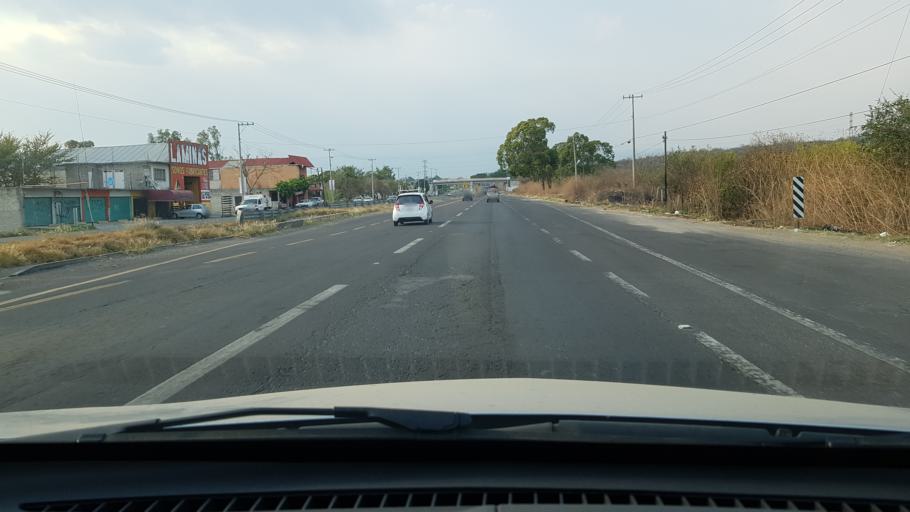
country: MX
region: Morelos
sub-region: Yecapixtla
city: Juan Morales
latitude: 18.8332
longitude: -98.9227
